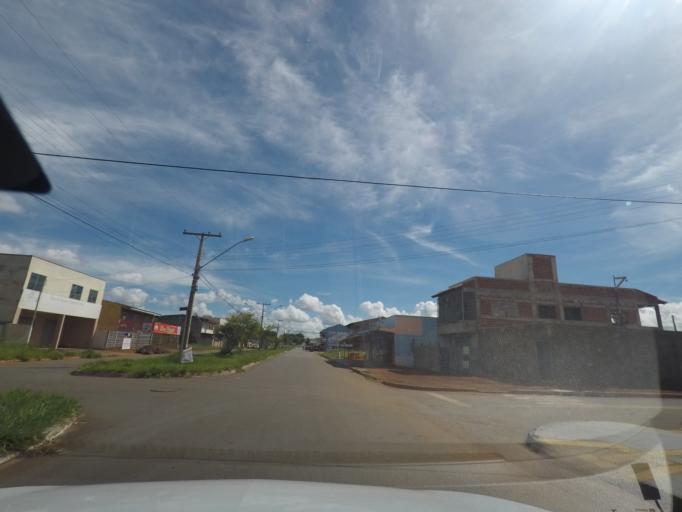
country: BR
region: Goias
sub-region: Goiania
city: Goiania
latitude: -16.7191
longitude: -49.3447
